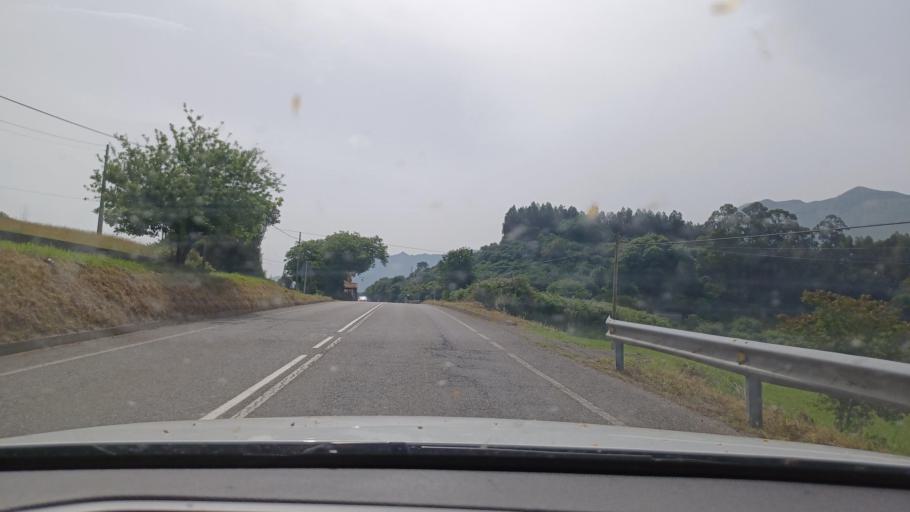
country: ES
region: Asturias
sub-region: Province of Asturias
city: Ribadesella
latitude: 43.4560
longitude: -5.0397
